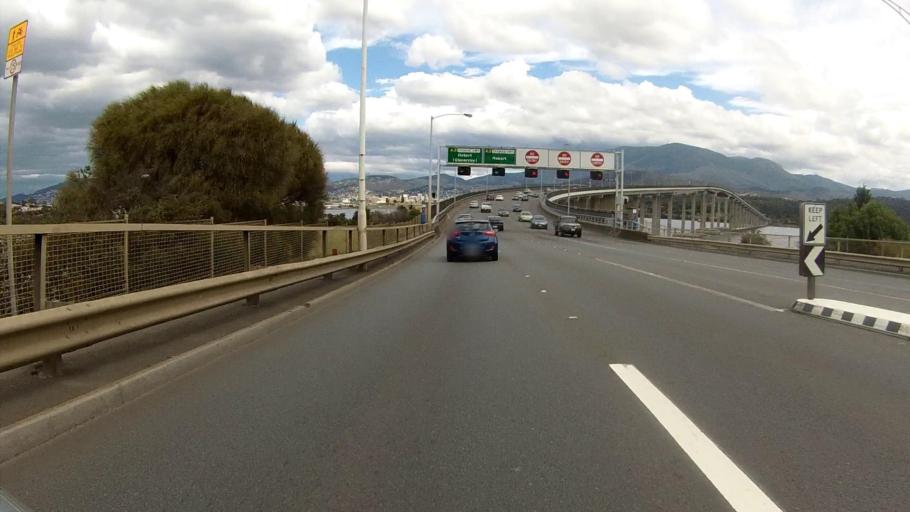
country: AU
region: Tasmania
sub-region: Clarence
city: Lindisfarne
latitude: -42.8630
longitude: 147.3532
